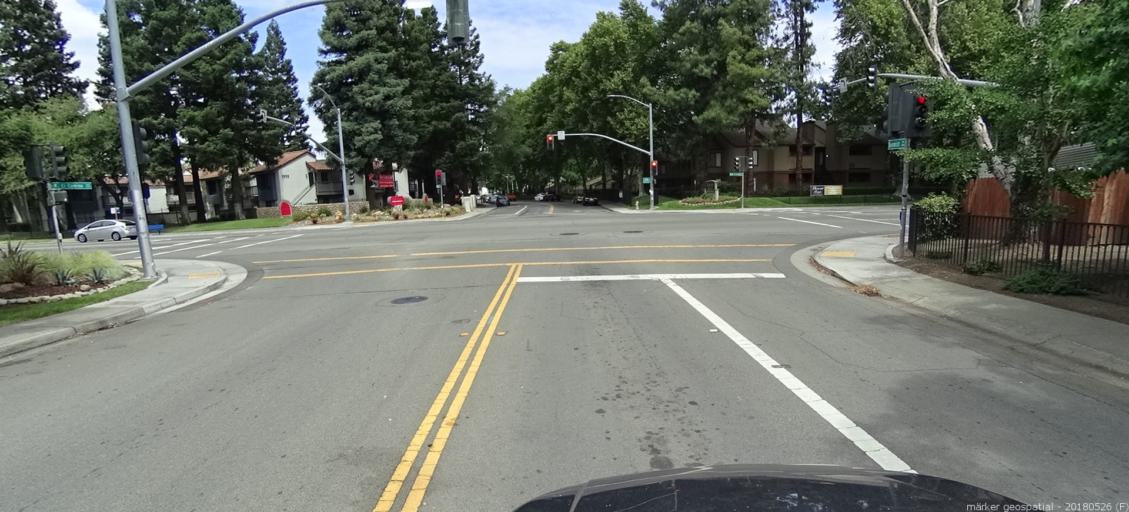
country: US
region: California
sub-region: Sacramento County
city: Sacramento
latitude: 38.6126
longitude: -121.4933
